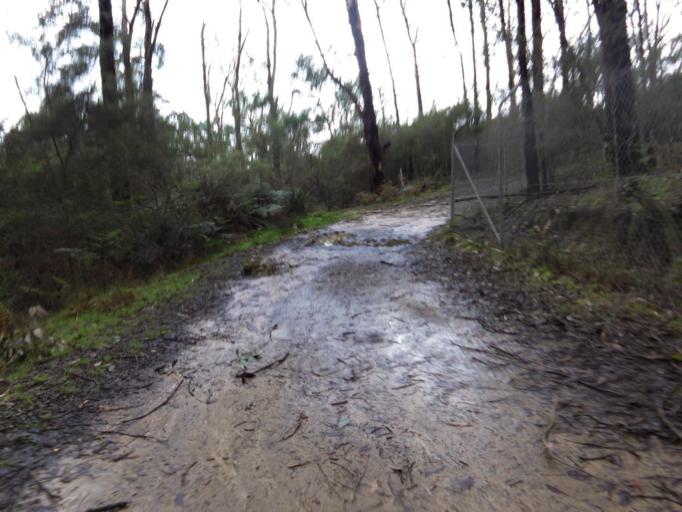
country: AU
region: Victoria
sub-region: Yarra Ranges
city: Lysterfield
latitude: -37.9324
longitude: 145.2817
